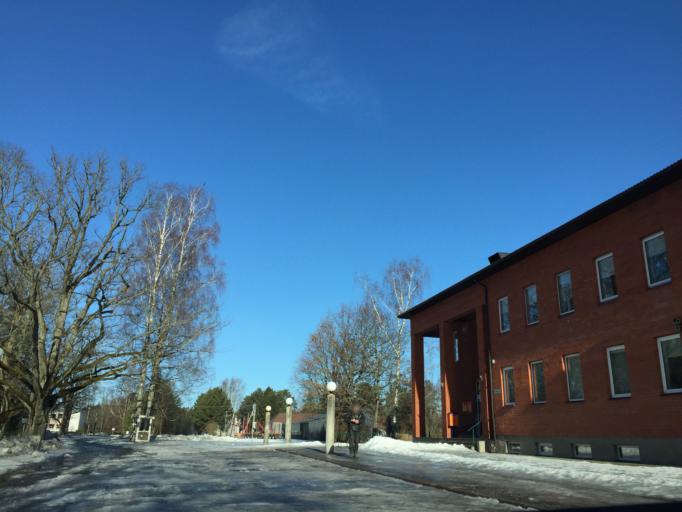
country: EE
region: Paernumaa
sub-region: Paikuse vald
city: Paikuse
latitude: 58.2787
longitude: 24.5781
